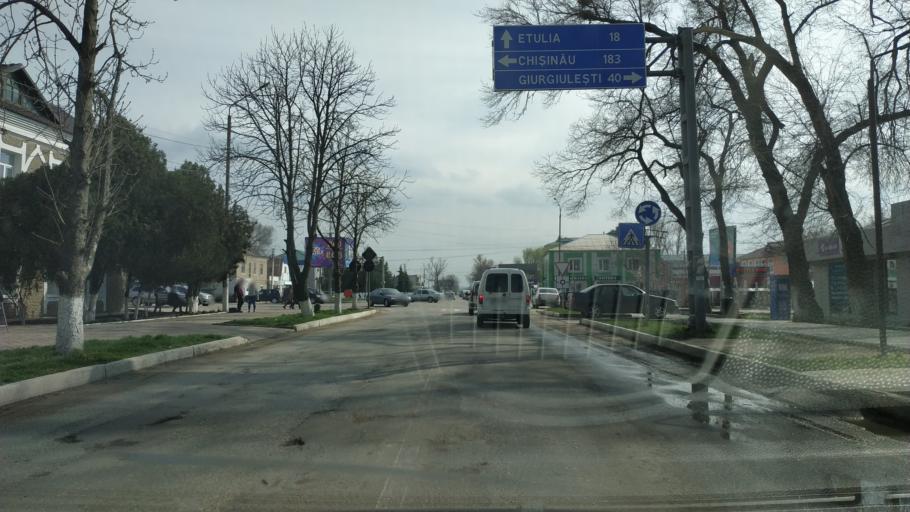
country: MD
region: Gagauzia
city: Vulcanesti
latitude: 45.6843
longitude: 28.4060
